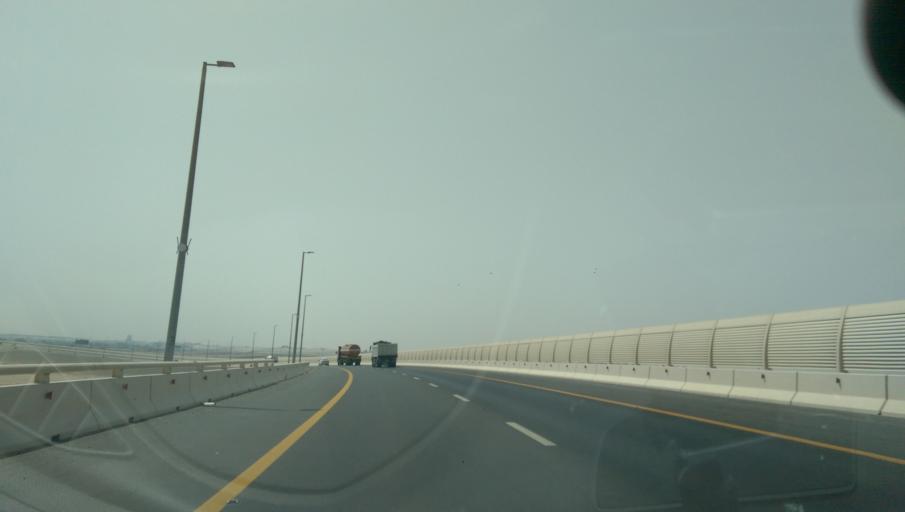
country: AE
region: Abu Dhabi
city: Abu Dhabi
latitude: 24.2860
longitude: 54.5490
